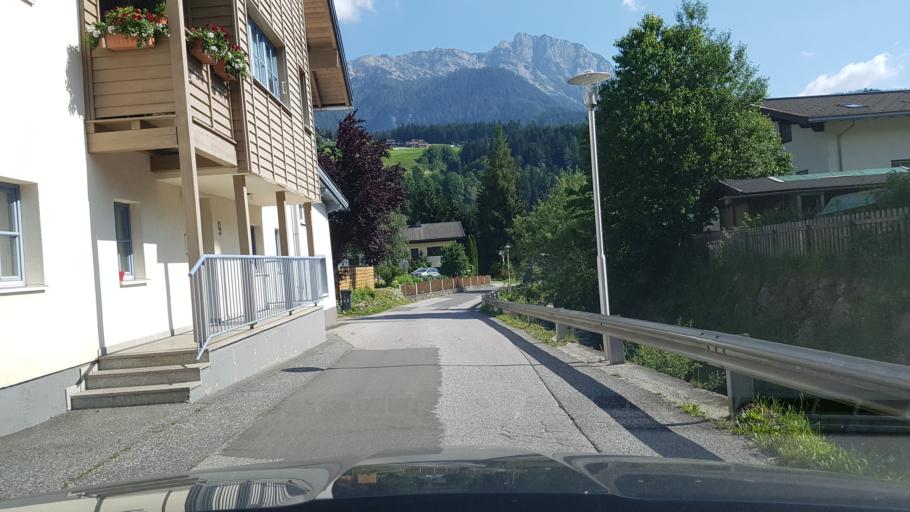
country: AT
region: Salzburg
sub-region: Politischer Bezirk Zell am See
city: Leogang
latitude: 47.4374
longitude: 12.7576
